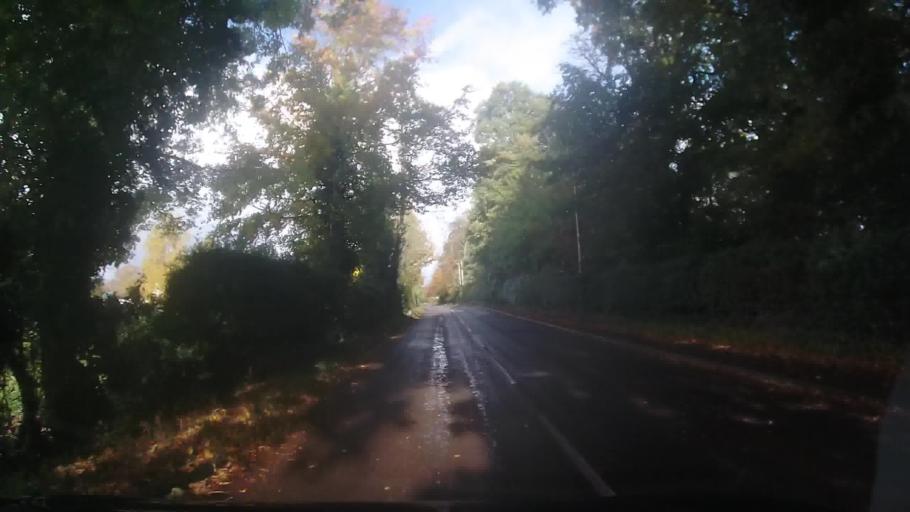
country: GB
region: England
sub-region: Shropshire
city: Whitchurch
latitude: 52.9586
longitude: -2.6793
